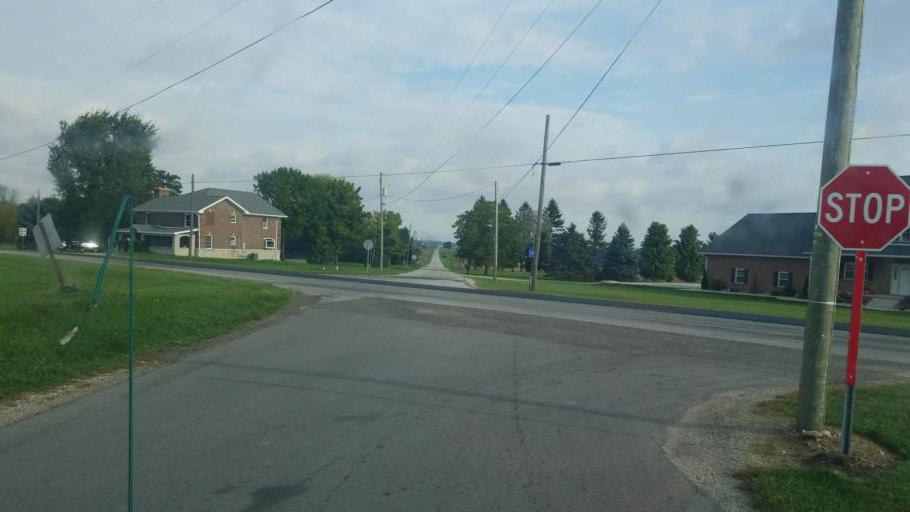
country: US
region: Ohio
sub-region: Wyandot County
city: Carey
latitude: 40.9688
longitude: -83.4293
